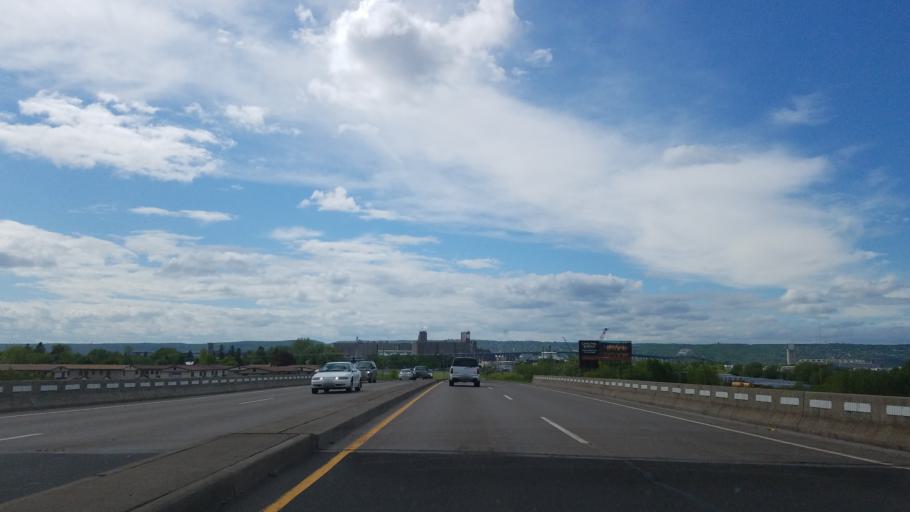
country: US
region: Wisconsin
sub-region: Douglas County
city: Superior
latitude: 46.7306
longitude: -92.0816
